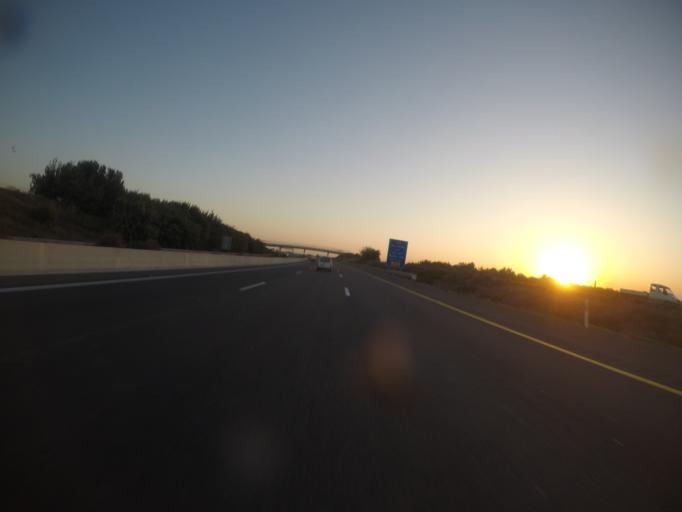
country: PS
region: West Bank
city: Nazlat `Isa
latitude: 32.4279
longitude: 35.0218
